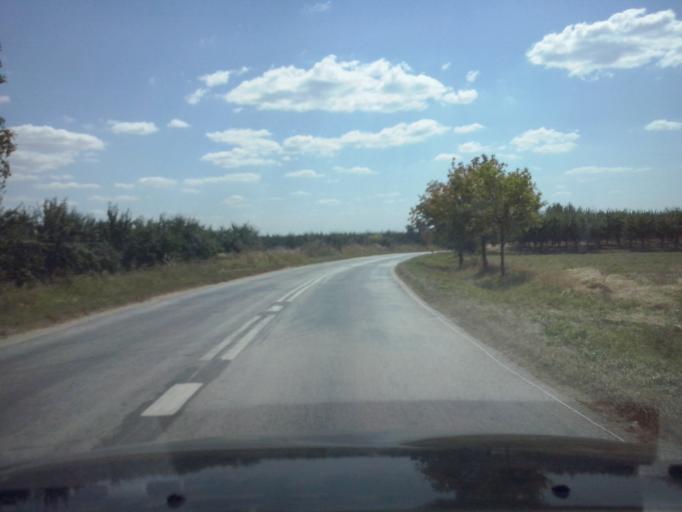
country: PL
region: Swietokrzyskie
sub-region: Powiat staszowski
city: Szydlow
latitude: 50.6074
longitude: 21.0097
